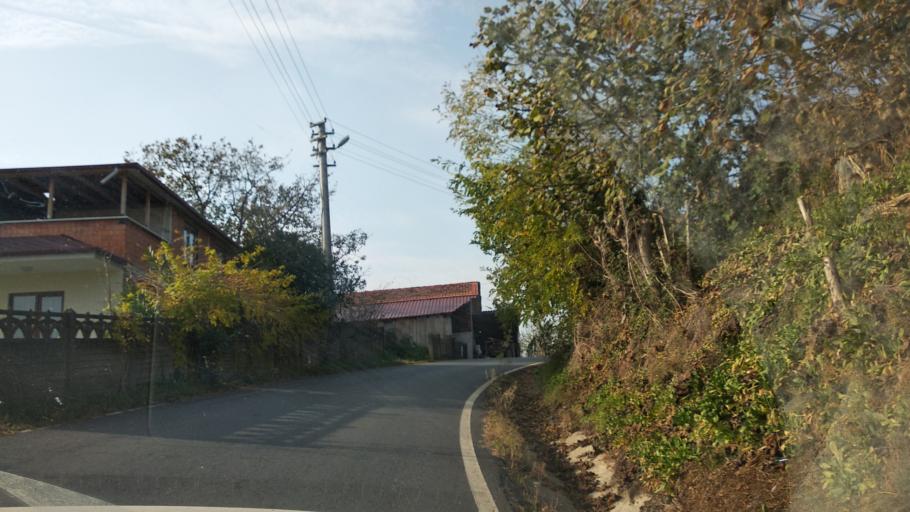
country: TR
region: Sakarya
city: Karasu
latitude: 41.0594
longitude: 30.6219
